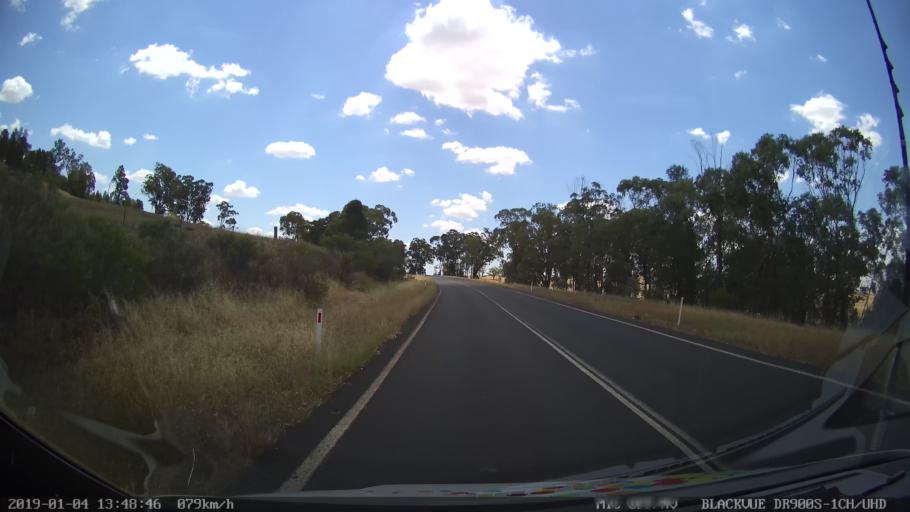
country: AU
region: New South Wales
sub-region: Dubbo Municipality
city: Dubbo
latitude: -32.4386
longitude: 148.5844
